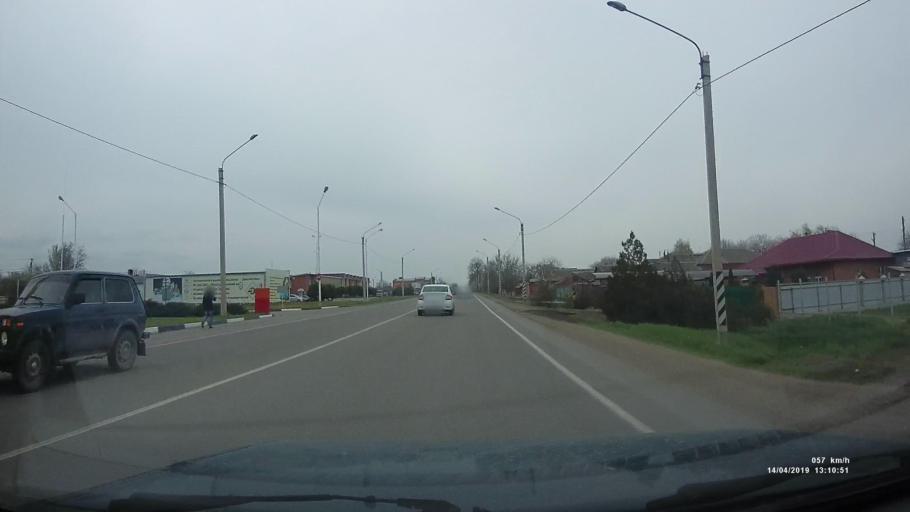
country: RU
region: Rostov
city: Kuleshovka
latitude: 47.1083
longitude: 39.6493
